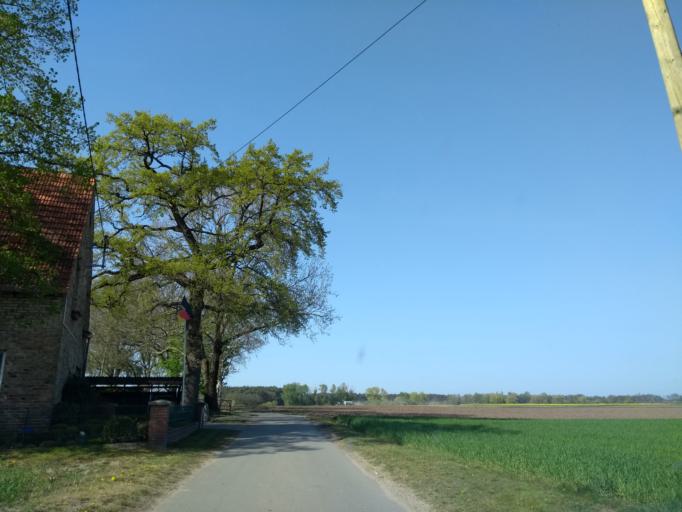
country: DE
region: North Rhine-Westphalia
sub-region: Regierungsbezirk Detmold
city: Delbruck
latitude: 51.7115
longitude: 8.5314
